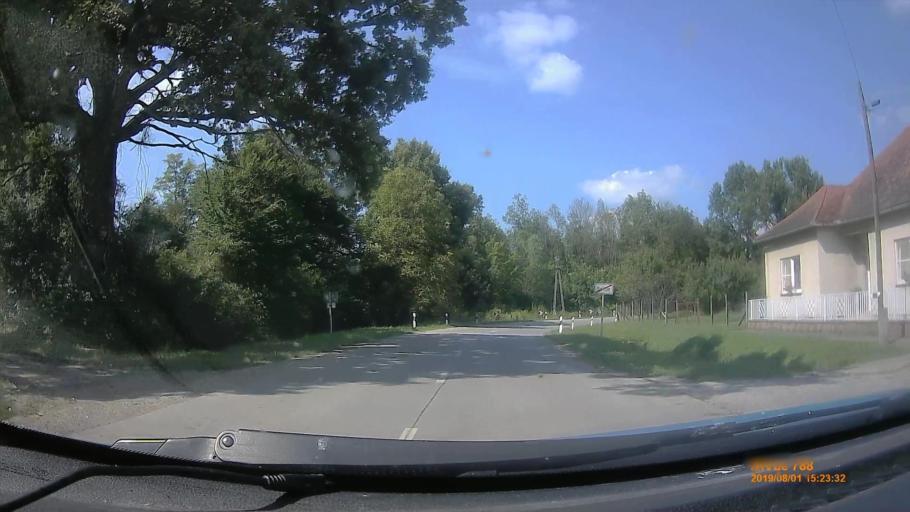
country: HU
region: Baranya
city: Sellye
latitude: 45.8785
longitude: 17.8446
